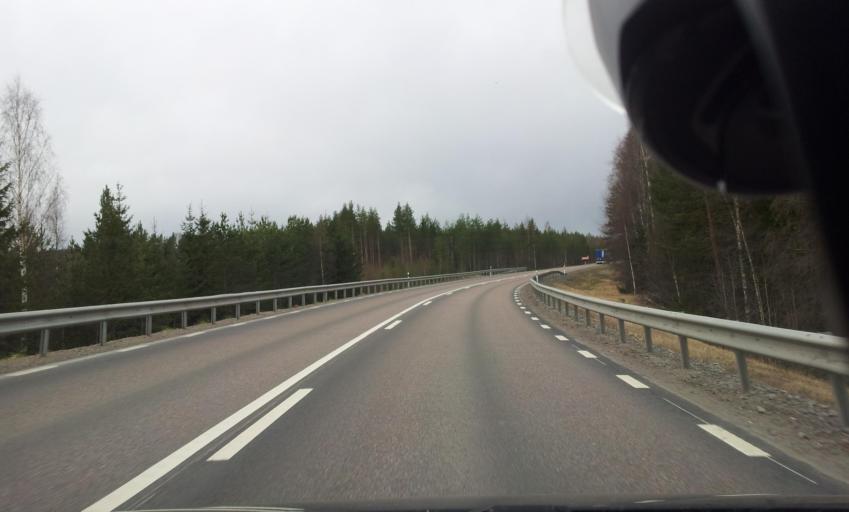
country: SE
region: Gaevleborg
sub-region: Ljusdals Kommun
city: Ljusdal
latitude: 61.8188
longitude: 16.0237
